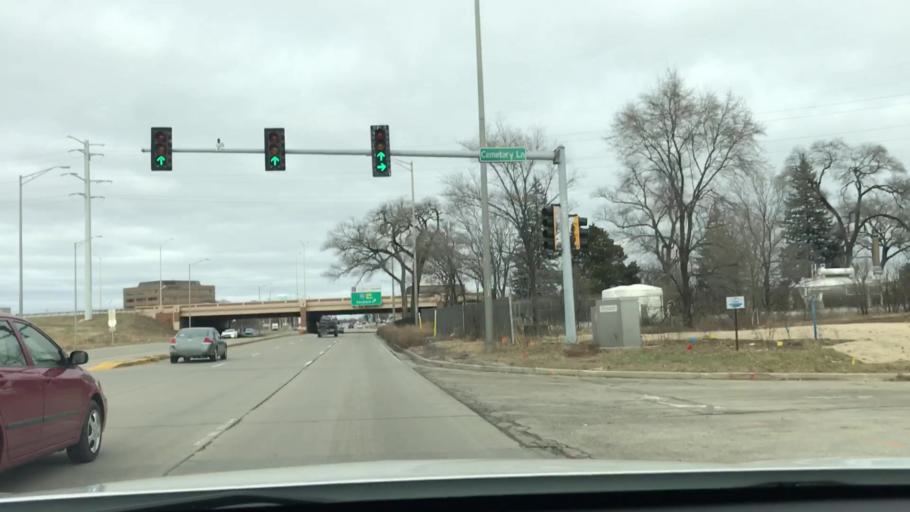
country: US
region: Illinois
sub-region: Cook County
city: Elk Grove Village
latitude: 42.0388
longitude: -87.9839
